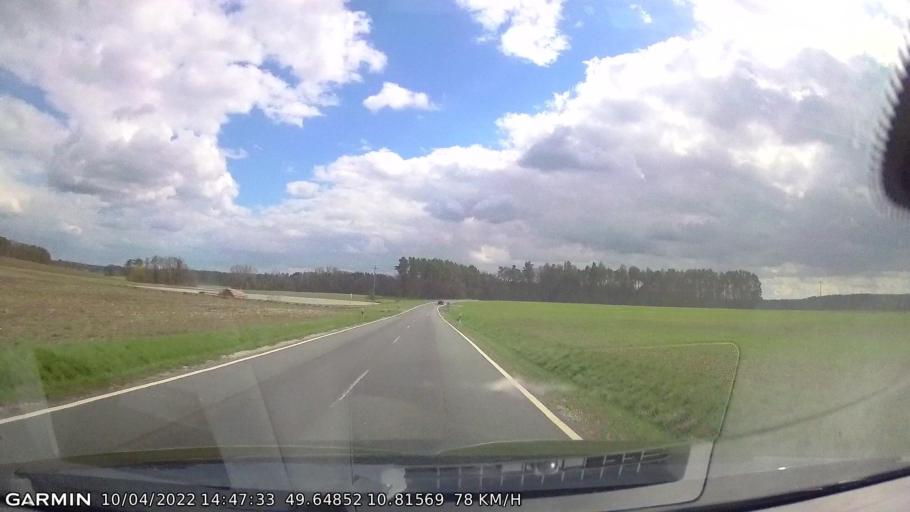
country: DE
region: Bavaria
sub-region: Regierungsbezirk Mittelfranken
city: Weisendorf
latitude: 49.6484
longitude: 10.8159
